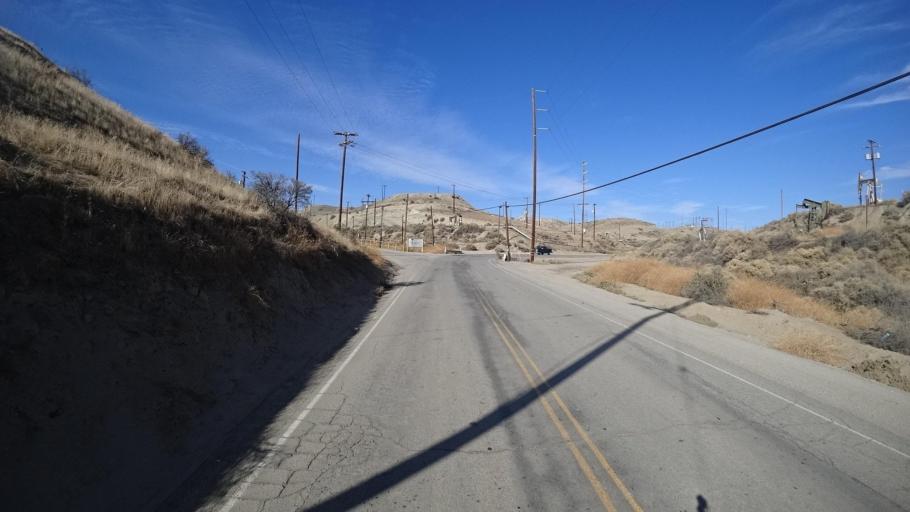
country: US
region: California
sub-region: Kern County
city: Oildale
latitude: 35.5881
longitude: -118.9605
